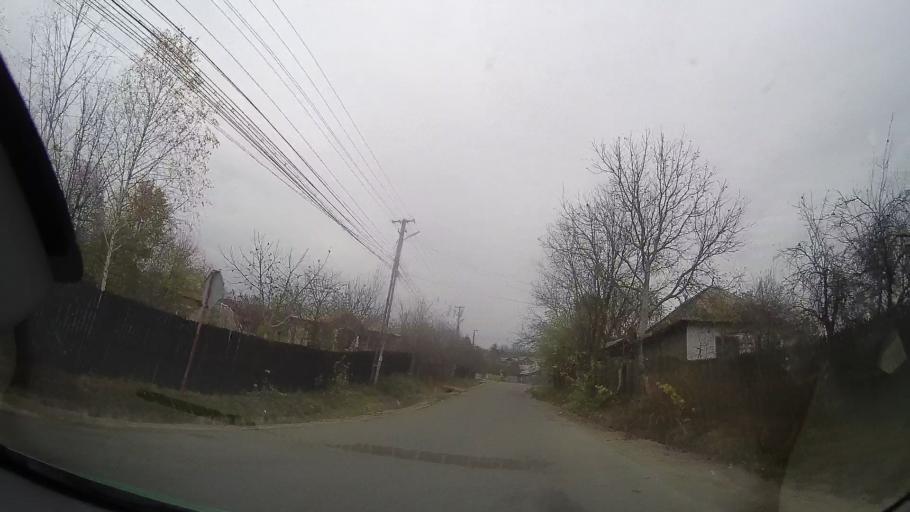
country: RO
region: Prahova
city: Mocesti
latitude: 45.0674
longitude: 26.2503
